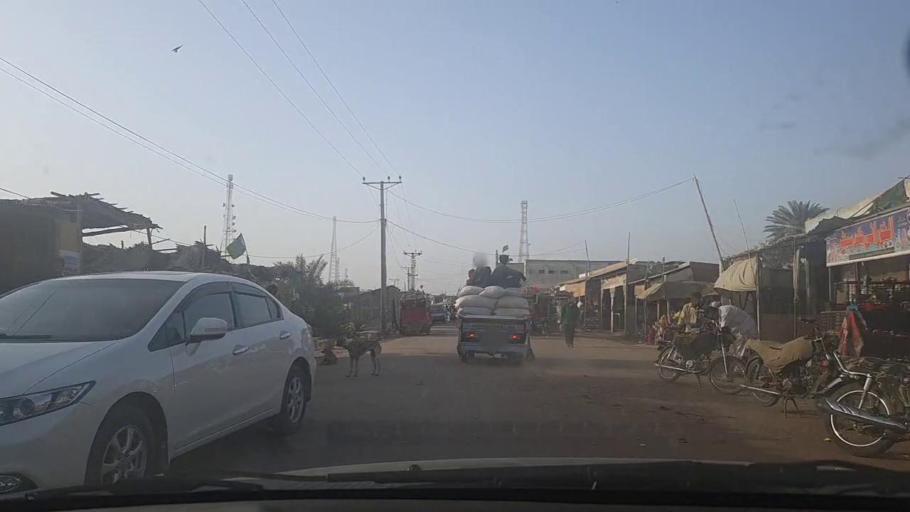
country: PK
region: Sindh
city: Keti Bandar
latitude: 24.2988
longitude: 67.6073
